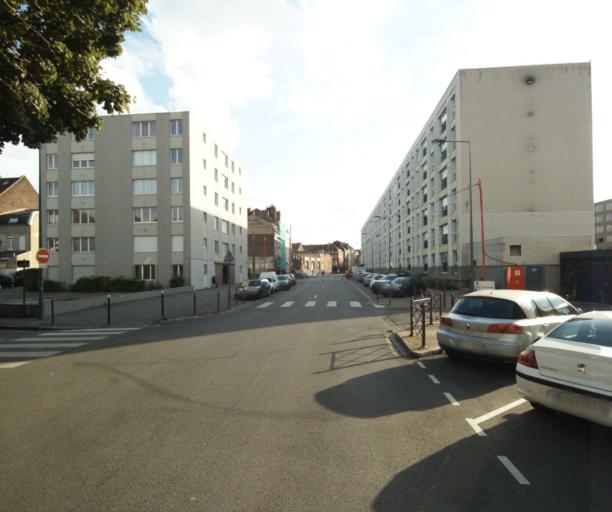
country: FR
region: Nord-Pas-de-Calais
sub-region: Departement du Nord
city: Lille
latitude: 50.6349
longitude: 3.0431
